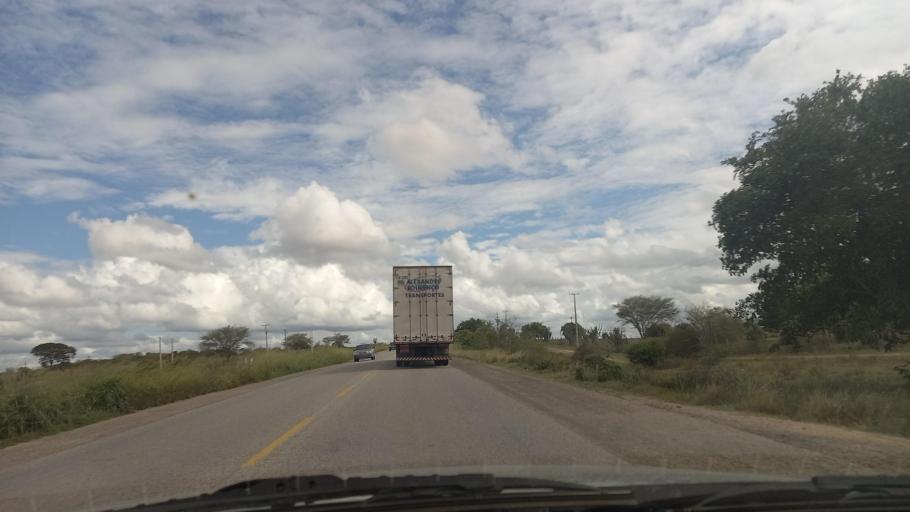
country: BR
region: Pernambuco
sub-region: Cachoeirinha
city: Cachoeirinha
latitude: -8.3992
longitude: -36.1828
